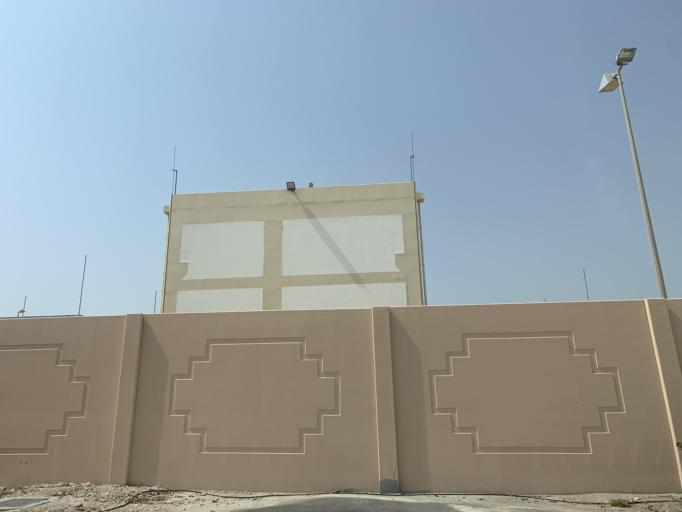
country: BH
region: Central Governorate
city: Madinat Hamad
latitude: 26.1657
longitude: 50.4815
